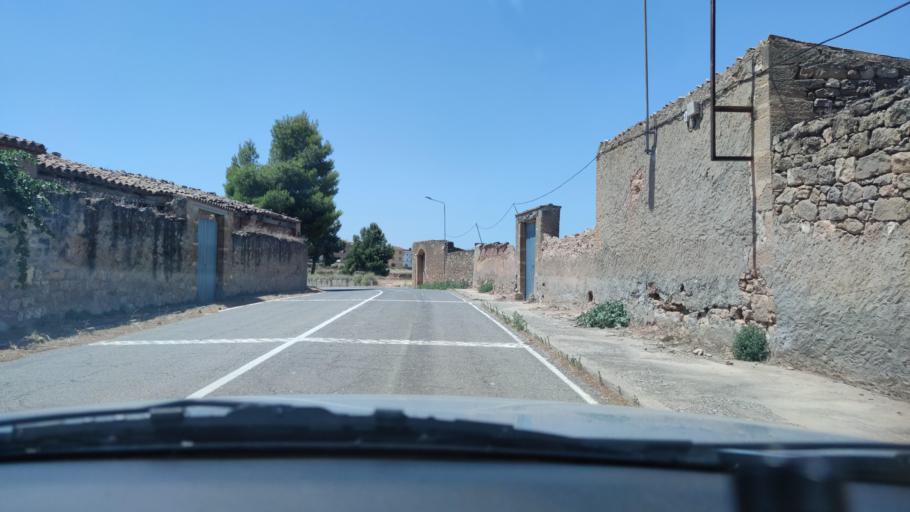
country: ES
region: Catalonia
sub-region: Provincia de Lleida
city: el Cogul
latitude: 41.4340
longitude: 0.6510
